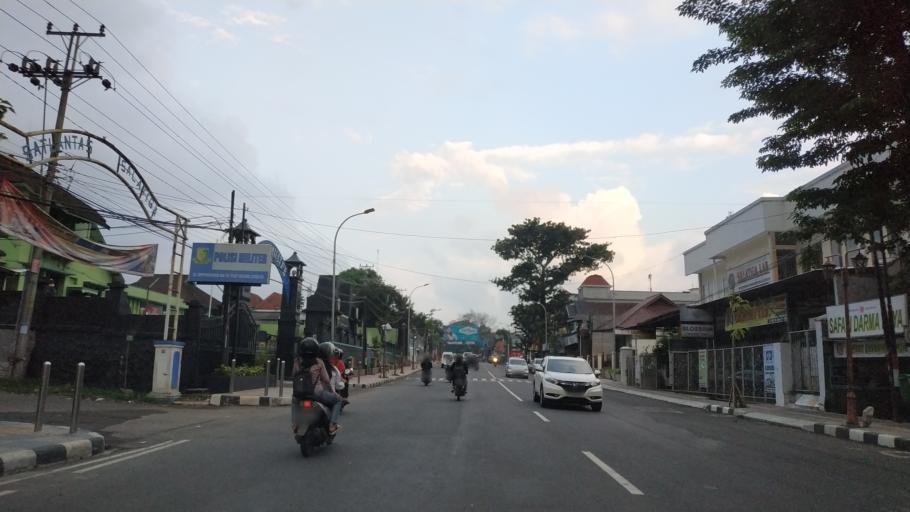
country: ID
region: Central Java
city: Salatiga
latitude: -7.3174
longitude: 110.4956
